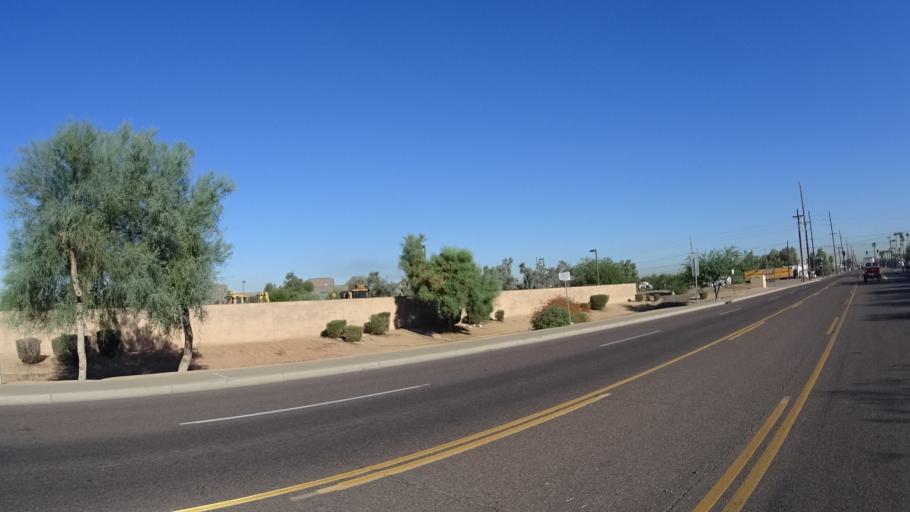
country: US
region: Arizona
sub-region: Maricopa County
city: Phoenix
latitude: 33.4279
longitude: -112.1172
